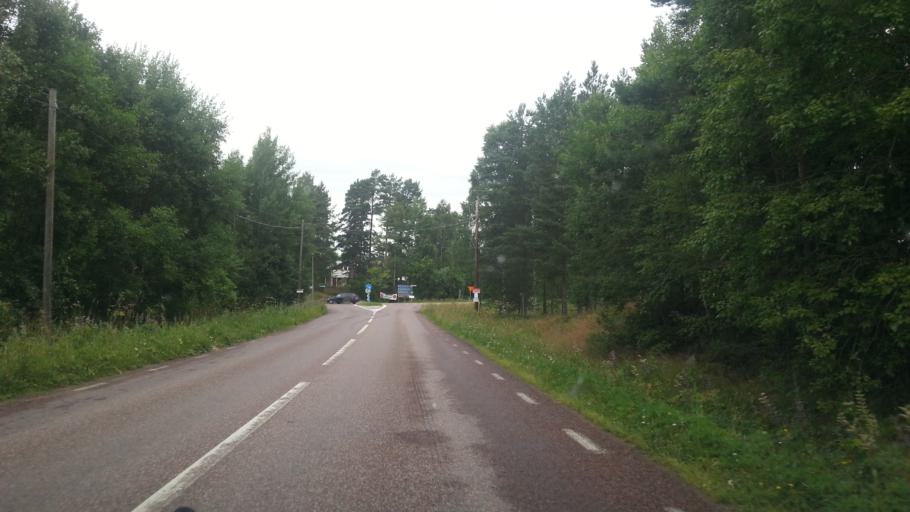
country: SE
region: Dalarna
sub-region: Faluns Kommun
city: Svardsjo
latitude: 60.6520
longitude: 15.7856
